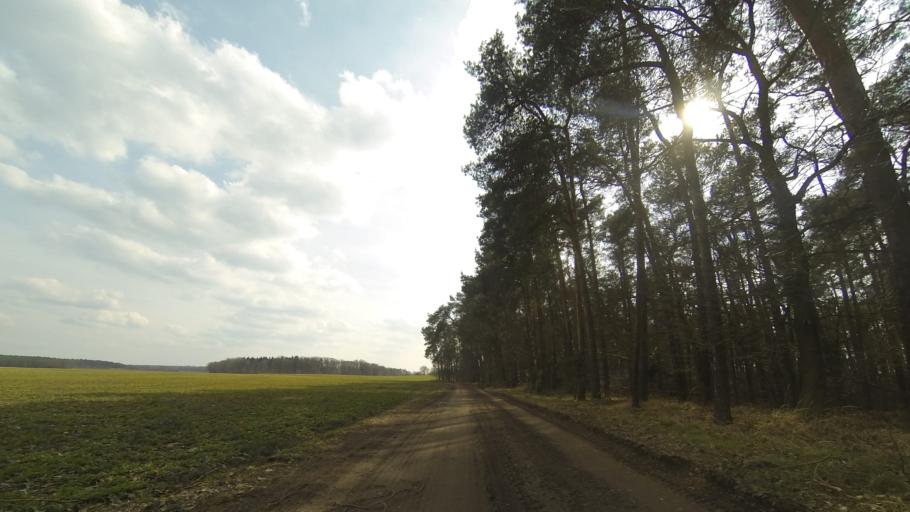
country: DE
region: Saxony
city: Schonfeld
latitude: 51.2541
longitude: 13.7017
